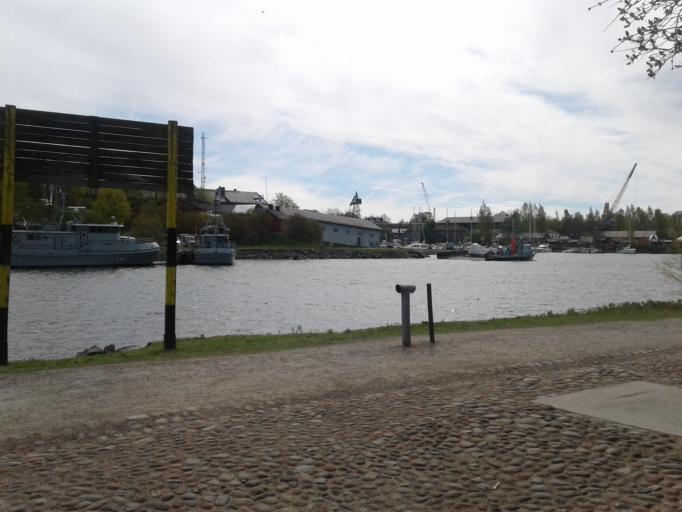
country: FI
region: Uusimaa
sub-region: Helsinki
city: Helsinki
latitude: 60.1489
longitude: 24.9807
